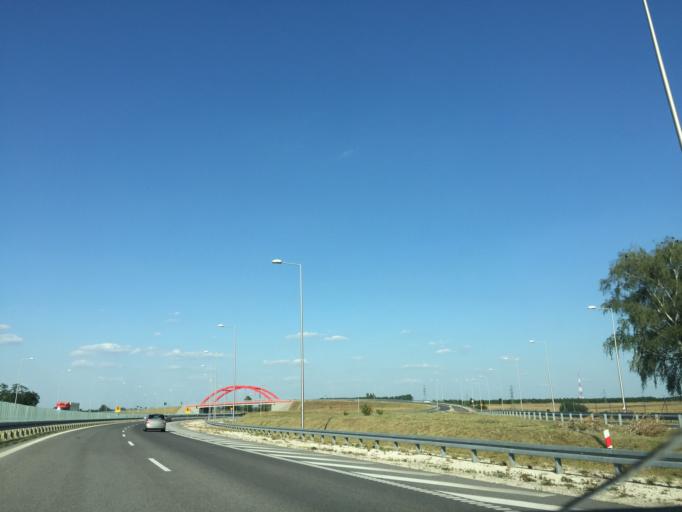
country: PL
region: Swietokrzyskie
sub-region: Powiat jedrzejowski
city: Jedrzejow
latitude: 50.6221
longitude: 20.2836
